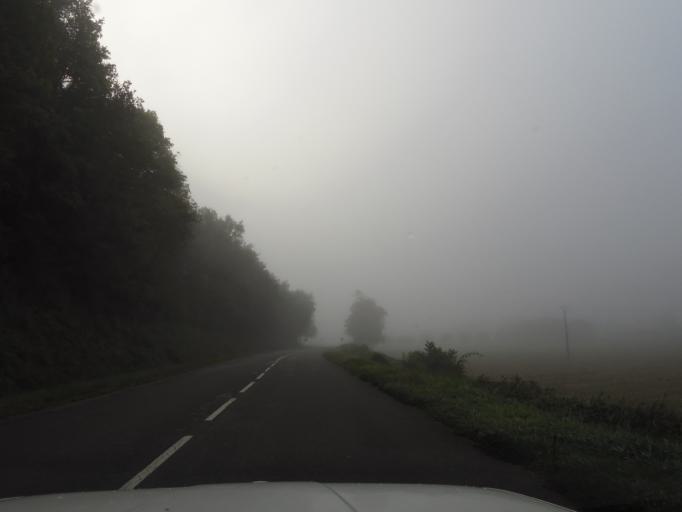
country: FR
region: Rhone-Alpes
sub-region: Departement de l'Isere
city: Creys-Mepieu
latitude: 45.7689
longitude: 5.4752
